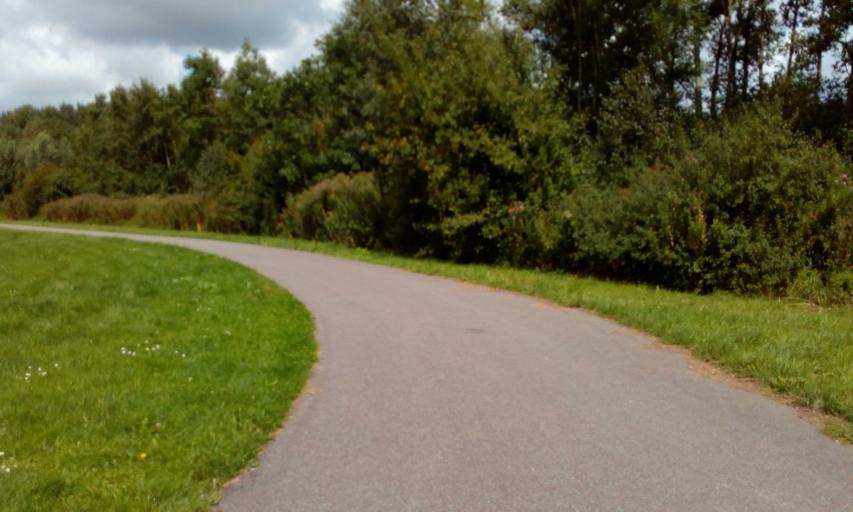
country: NL
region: South Holland
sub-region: Gemeente Barendrecht
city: Barendrecht
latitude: 51.8679
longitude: 4.5020
